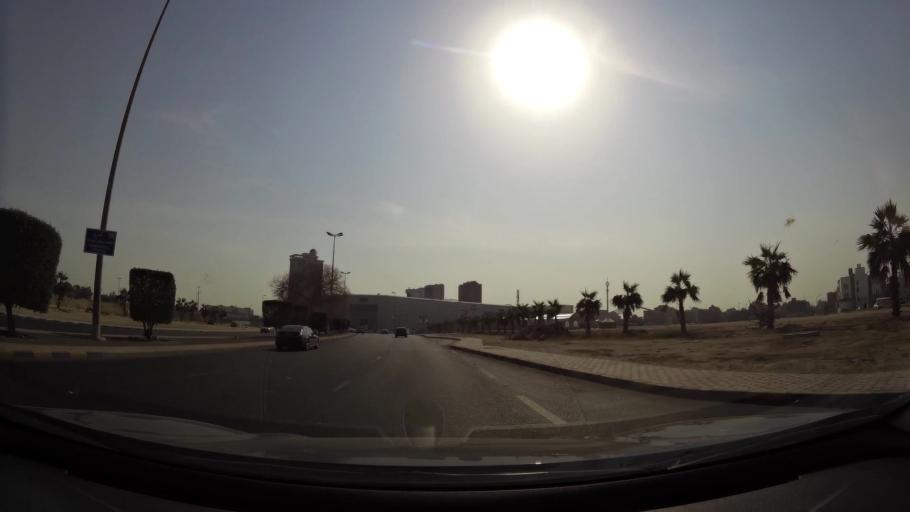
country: KW
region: Mubarak al Kabir
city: Mubarak al Kabir
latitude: 29.1780
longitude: 48.1004
